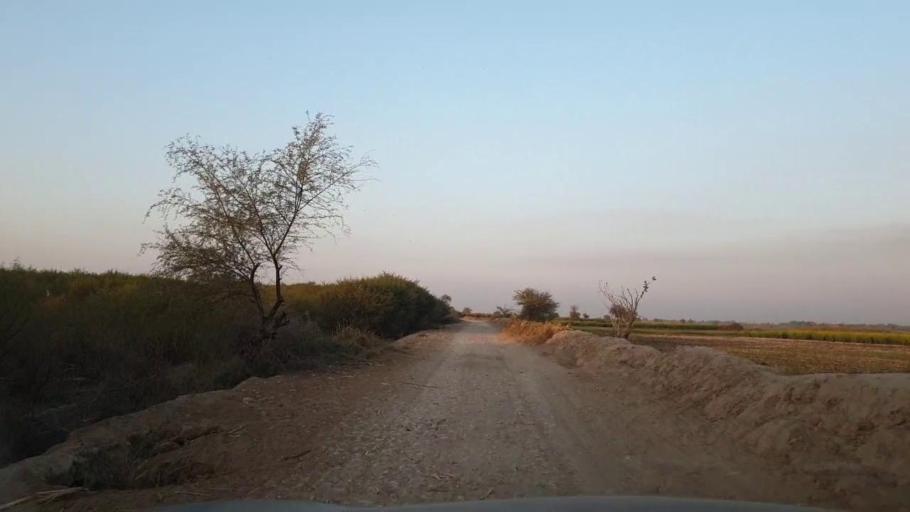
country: PK
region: Sindh
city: Berani
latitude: 25.6621
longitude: 68.7699
